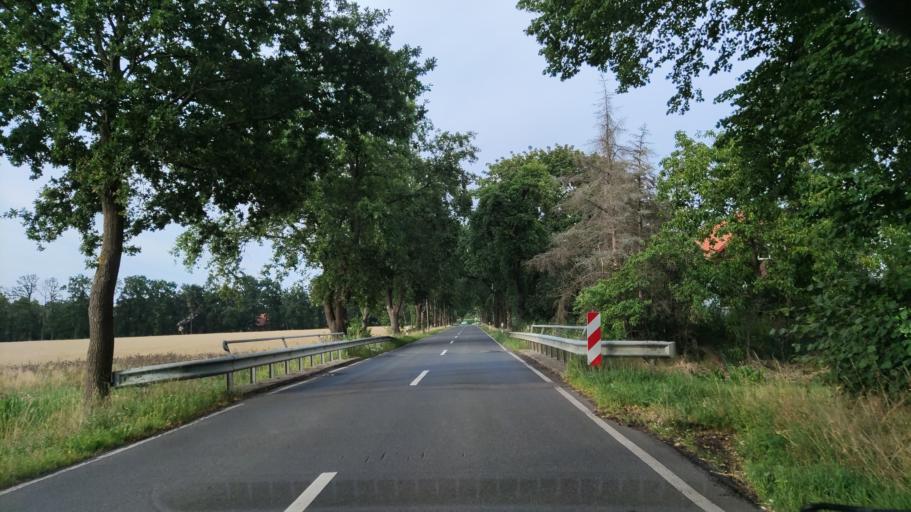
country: DE
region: Lower Saxony
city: Jameln
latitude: 53.0517
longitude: 11.1354
